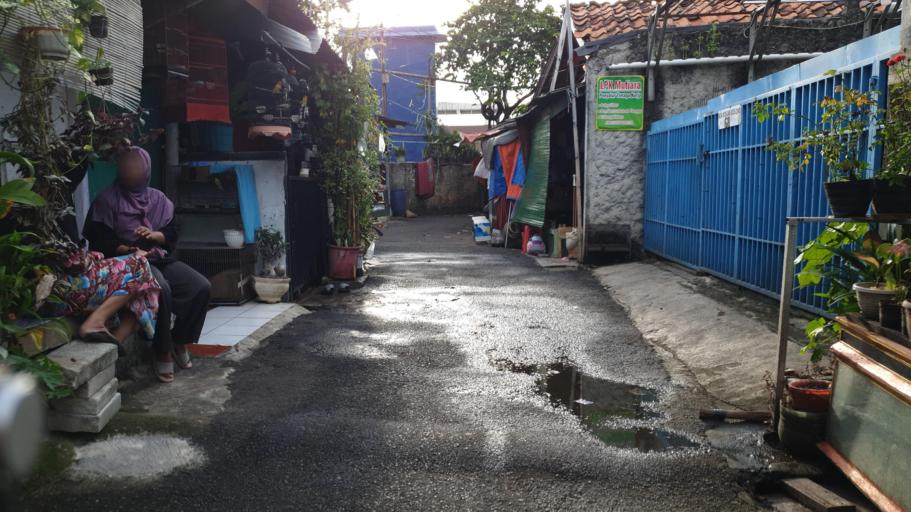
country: ID
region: Banten
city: South Tangerang
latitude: -6.2877
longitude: 106.7893
